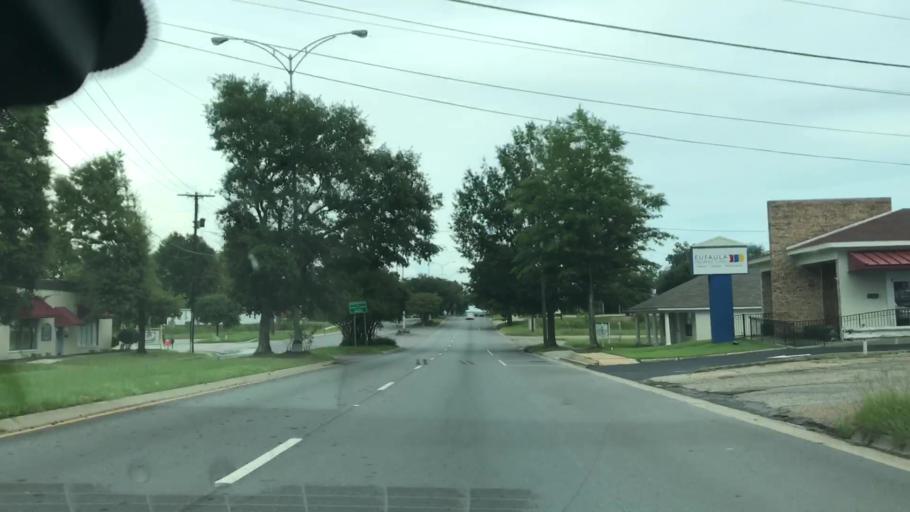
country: US
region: Alabama
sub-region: Barbour County
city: Eufaula
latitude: 31.8914
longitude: -85.1417
